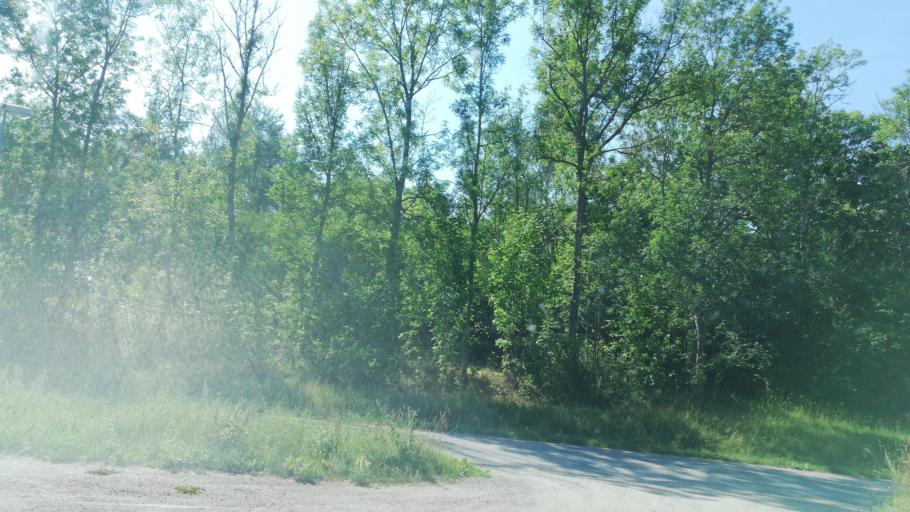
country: SE
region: OEstergoetland
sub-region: Finspangs Kommun
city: Finspang
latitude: 58.7358
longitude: 15.8230
